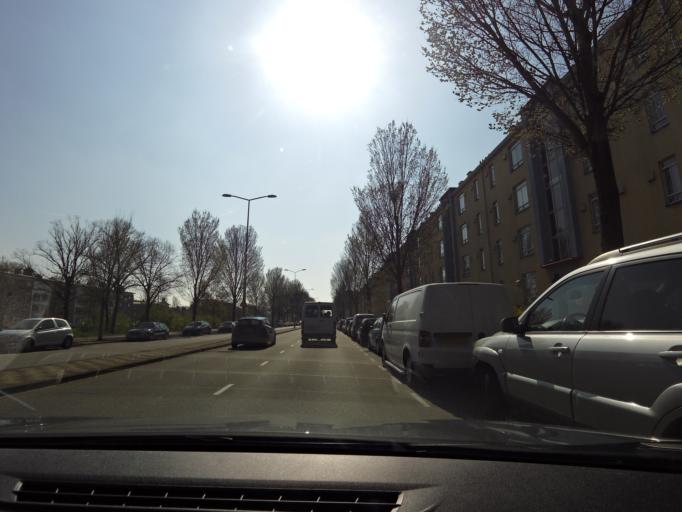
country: NL
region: South Holland
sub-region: Gemeente Den Haag
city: The Hague
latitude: 52.0541
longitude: 4.3060
